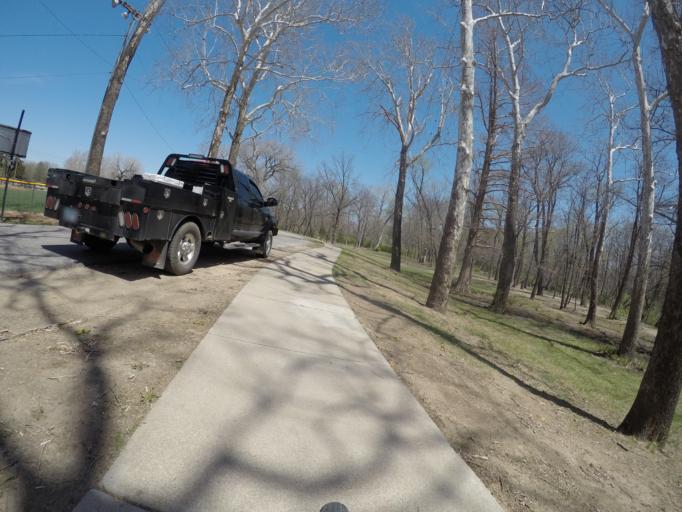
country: US
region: Kansas
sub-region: Pratt County
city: Pratt
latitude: 37.6342
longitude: -98.7316
